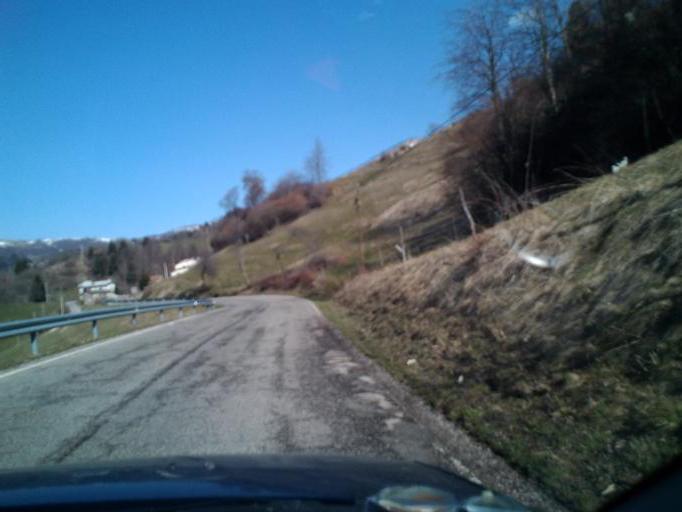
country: IT
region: Veneto
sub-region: Provincia di Verona
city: Bosco Chiesanuova
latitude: 45.6421
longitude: 11.0264
